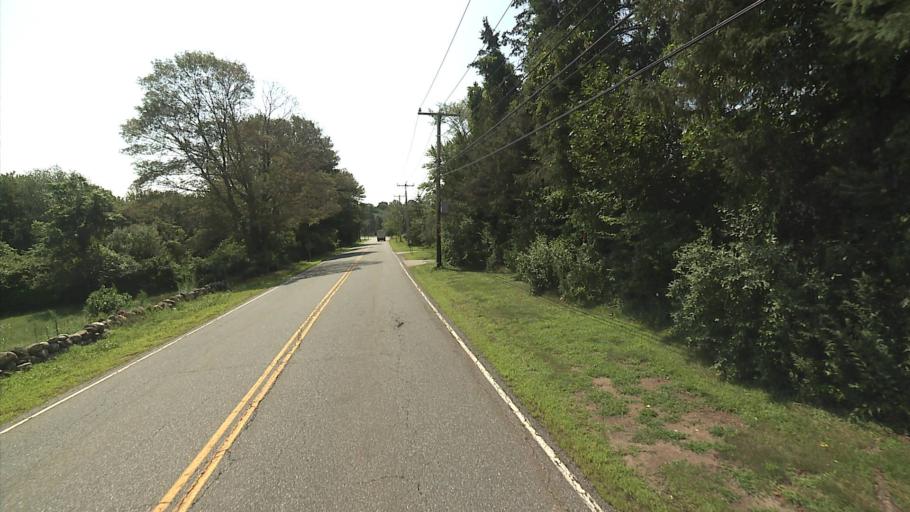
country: US
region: Connecticut
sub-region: New London County
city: Montville Center
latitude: 41.5094
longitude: -72.2480
